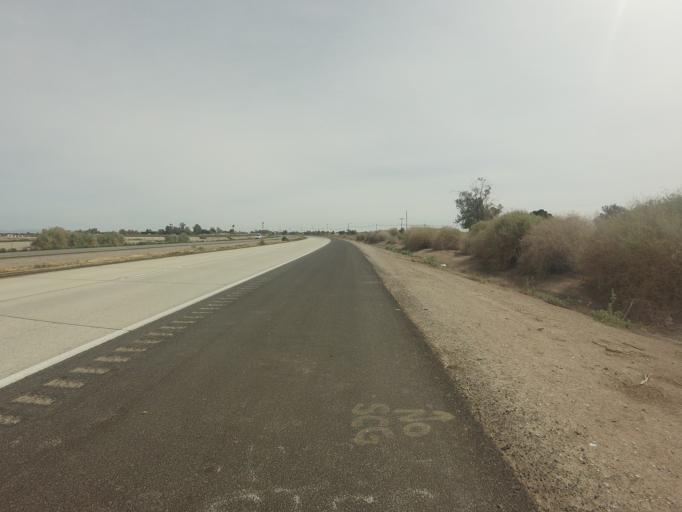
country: US
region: California
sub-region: Imperial County
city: Brawley
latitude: 32.9800
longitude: -115.5711
